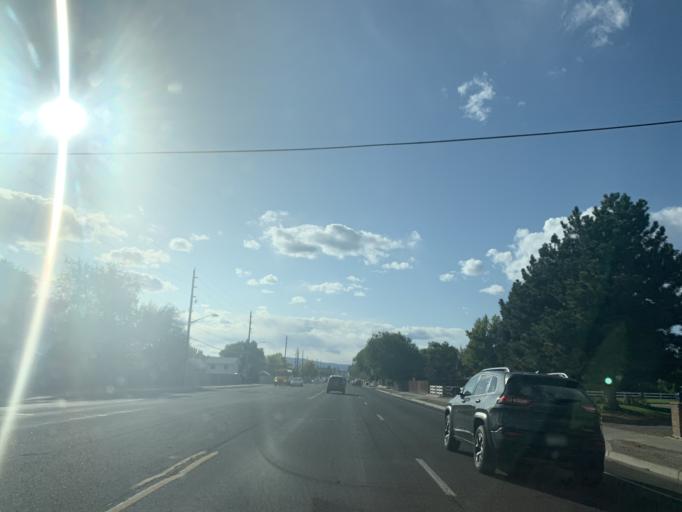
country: US
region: Colorado
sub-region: Mesa County
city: Fruitvale
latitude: 39.0918
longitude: -108.5098
